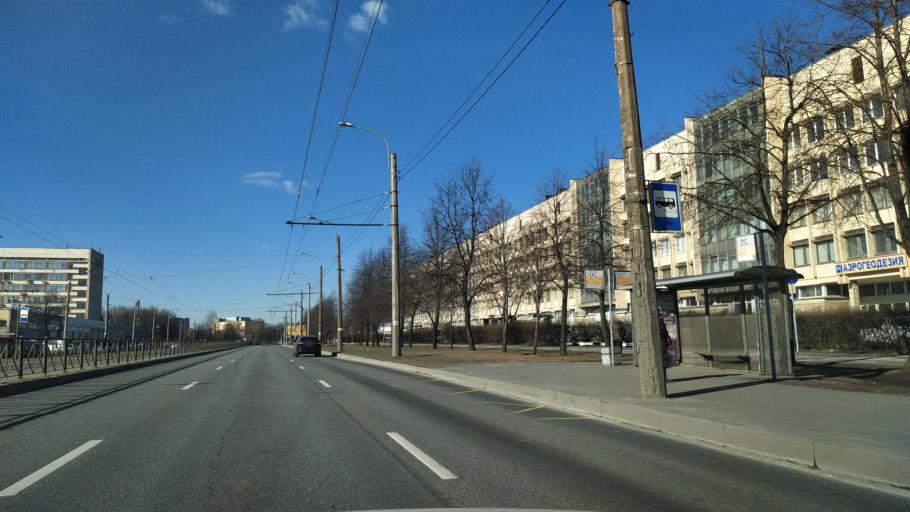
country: RU
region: St.-Petersburg
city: Kupchino
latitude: 59.8908
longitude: 30.3604
